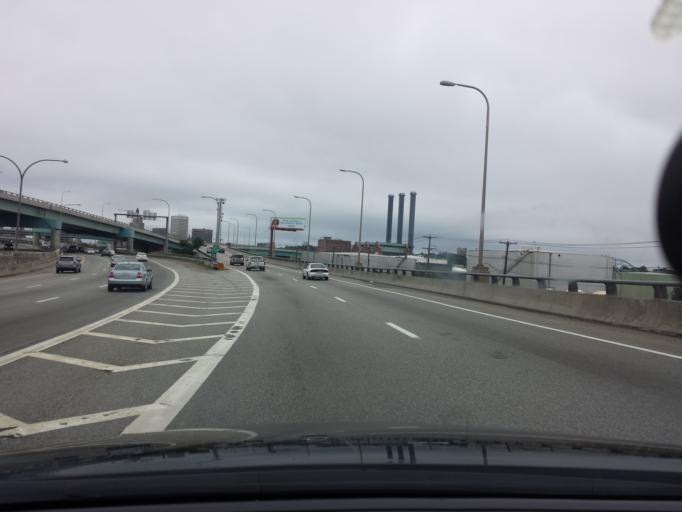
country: US
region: Rhode Island
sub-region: Providence County
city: Providence
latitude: 41.8095
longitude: -71.4047
